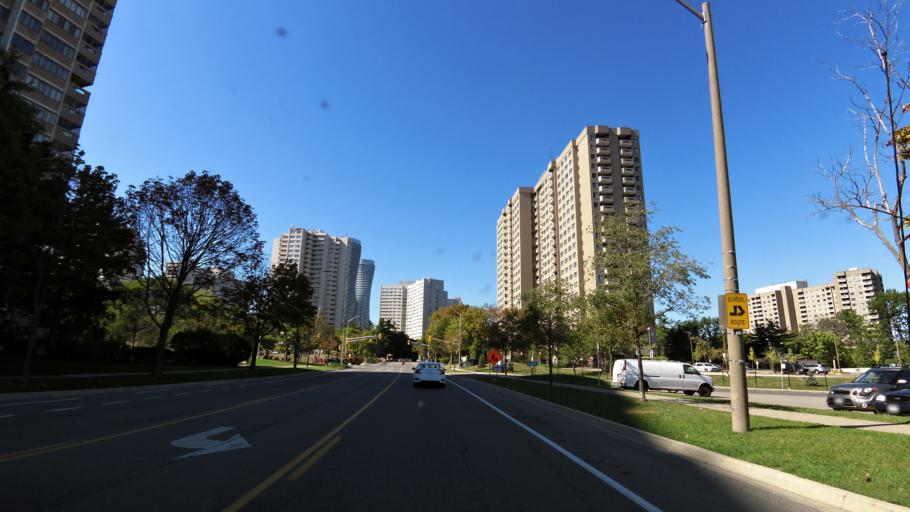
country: CA
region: Ontario
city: Mississauga
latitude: 43.5918
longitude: -79.6273
